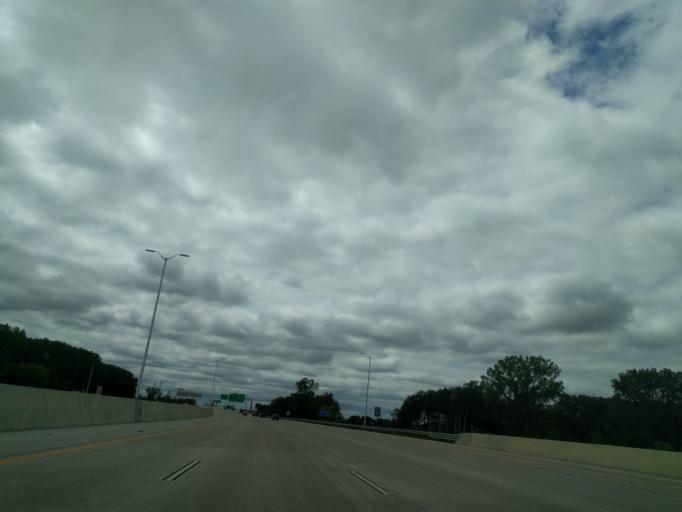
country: US
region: Wisconsin
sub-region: Brown County
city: Howard
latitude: 44.5539
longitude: -88.0641
